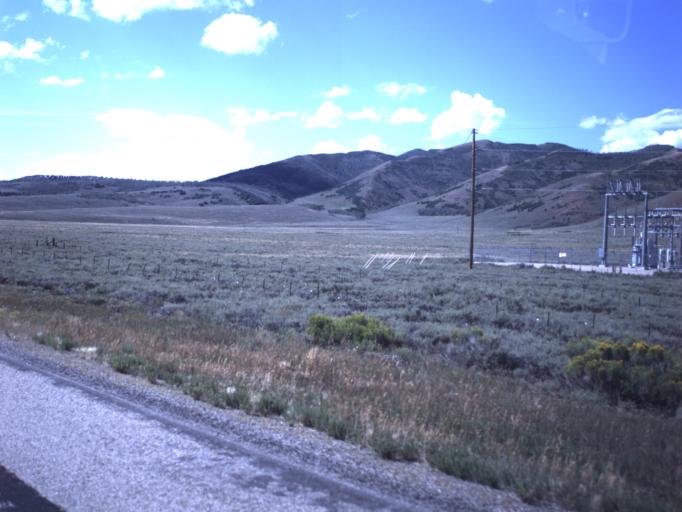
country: US
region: Utah
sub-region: Wasatch County
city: Heber
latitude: 40.2250
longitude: -111.1089
